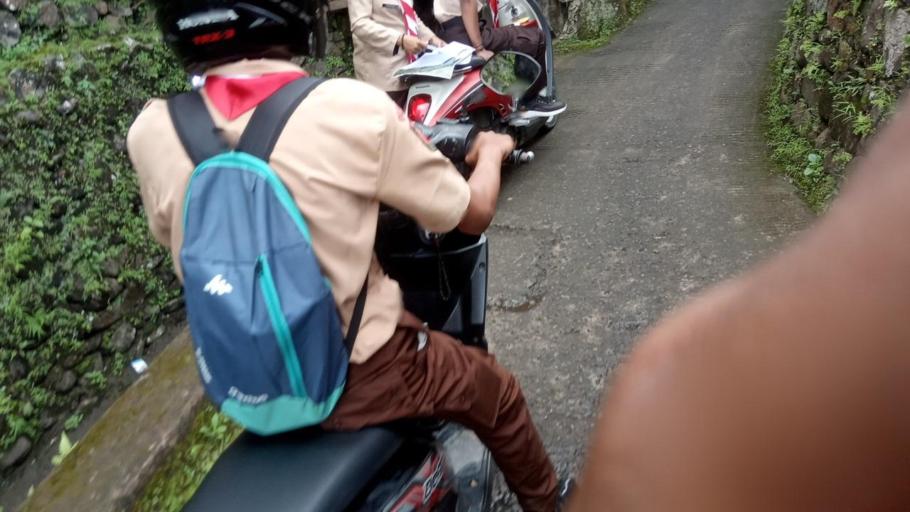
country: ID
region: West Java
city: Caringin
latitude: -6.6492
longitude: 106.8930
